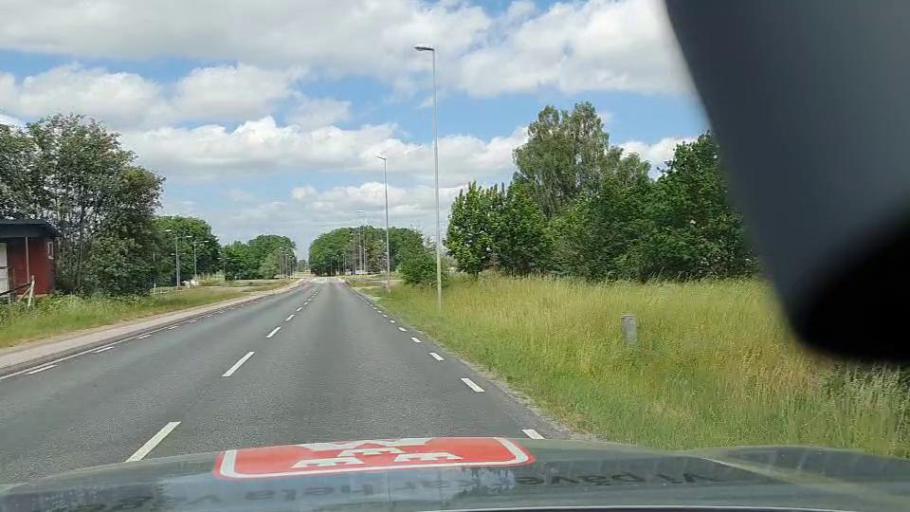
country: SE
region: Blekinge
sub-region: Karlshamns Kommun
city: Morrum
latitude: 56.1152
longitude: 14.6758
